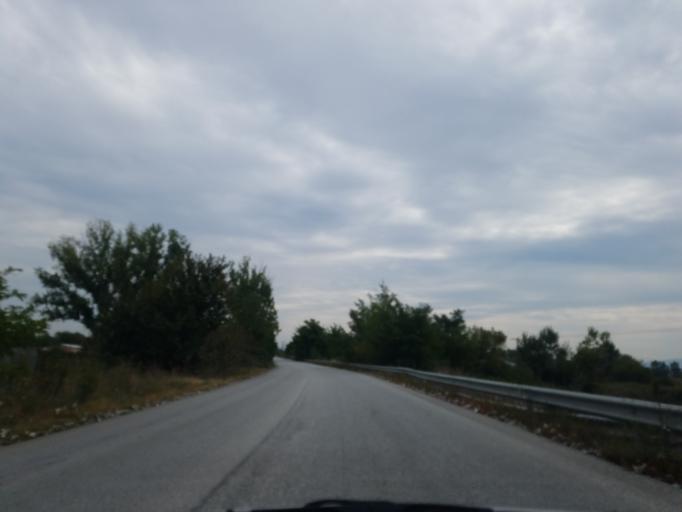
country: GR
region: Thessaly
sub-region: Nomos Kardhitsas
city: Sofades
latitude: 39.3288
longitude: 22.0891
